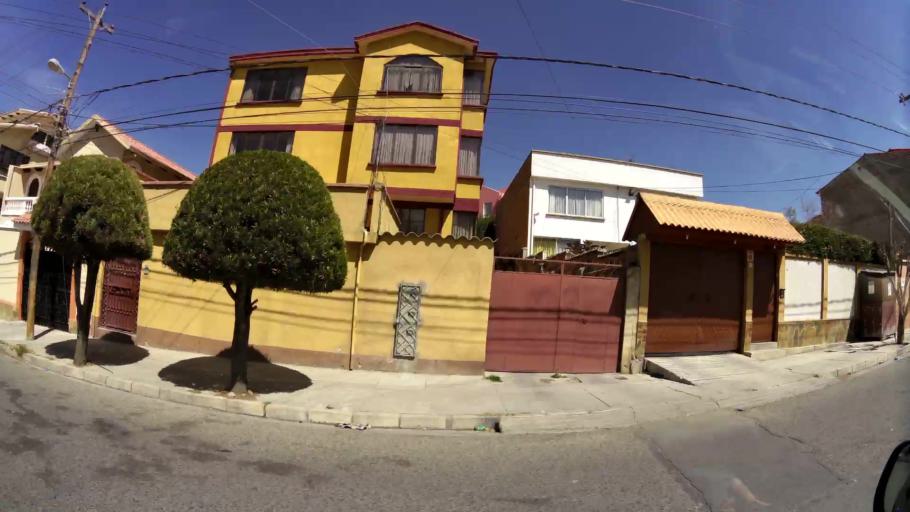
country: BO
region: La Paz
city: La Paz
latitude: -16.5328
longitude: -68.1041
